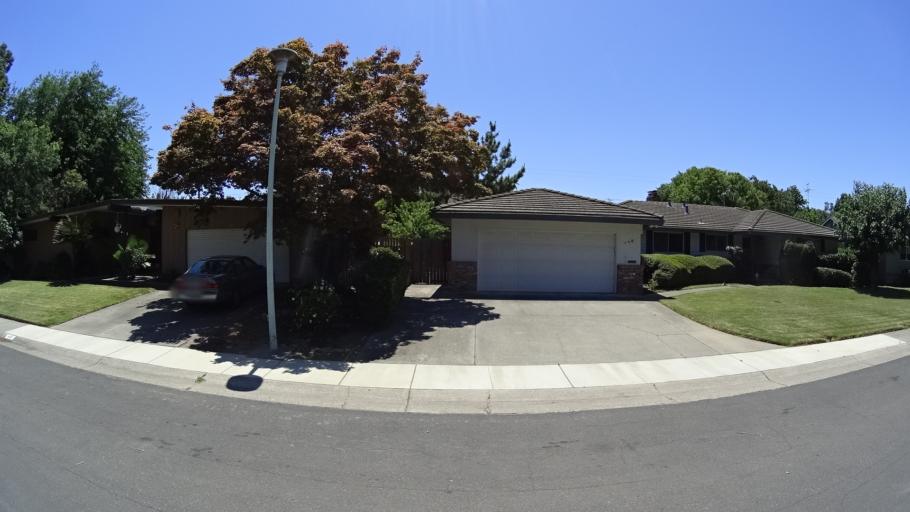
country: US
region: California
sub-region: Yolo County
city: West Sacramento
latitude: 38.5270
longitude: -121.5242
